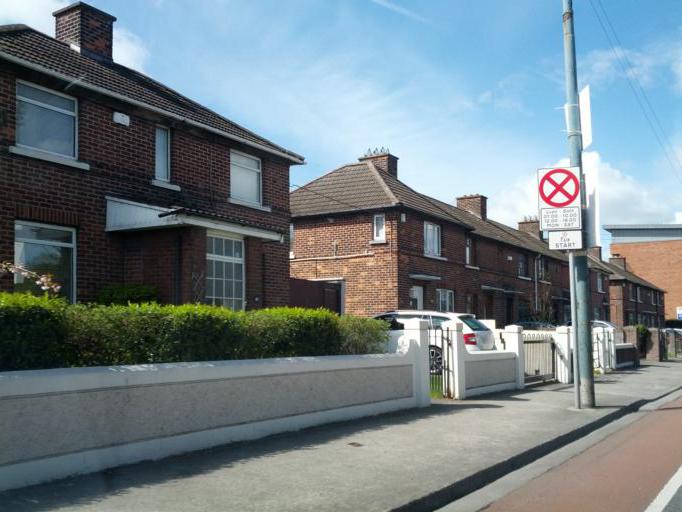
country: IE
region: Leinster
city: Rialto
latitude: 53.3305
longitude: -6.2843
